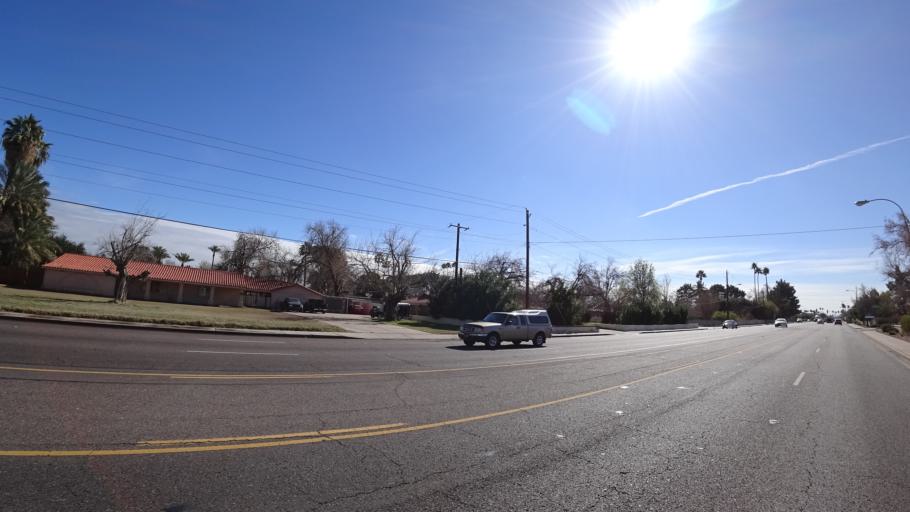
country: US
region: Arizona
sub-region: Maricopa County
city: Glendale
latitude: 33.5557
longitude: -112.1863
